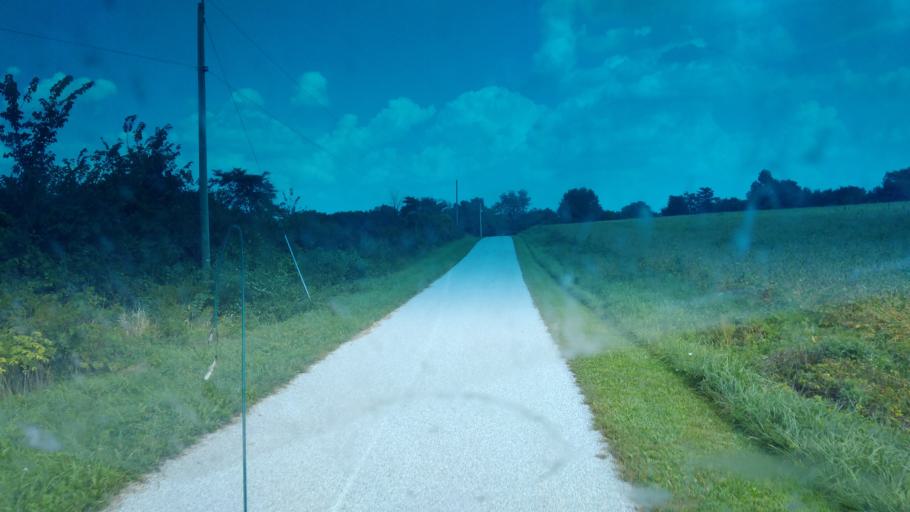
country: US
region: Ohio
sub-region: Hardin County
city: Ada
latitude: 40.7152
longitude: -83.7701
